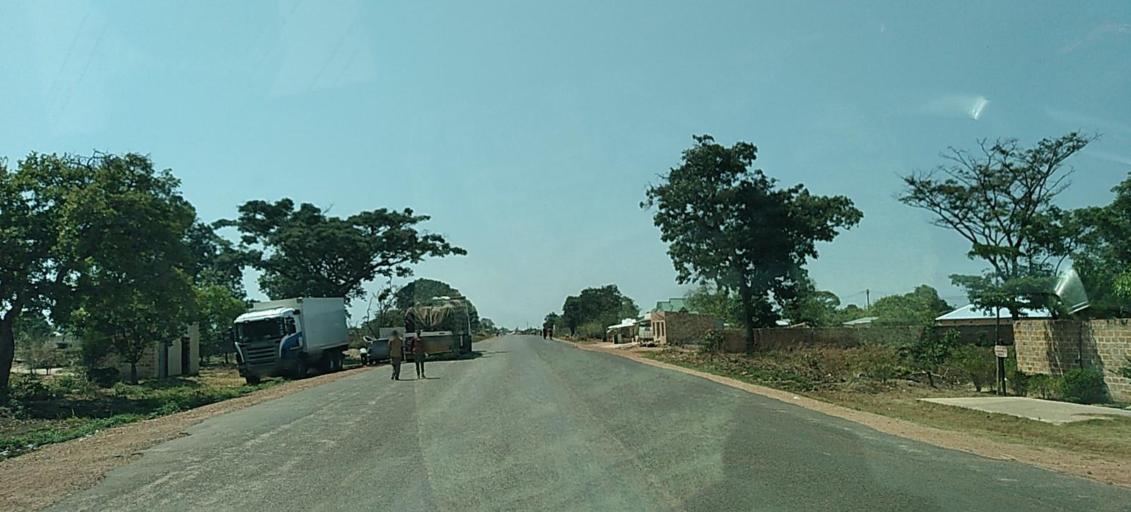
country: ZM
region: North-Western
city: Solwezi
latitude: -12.3077
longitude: 25.8399
